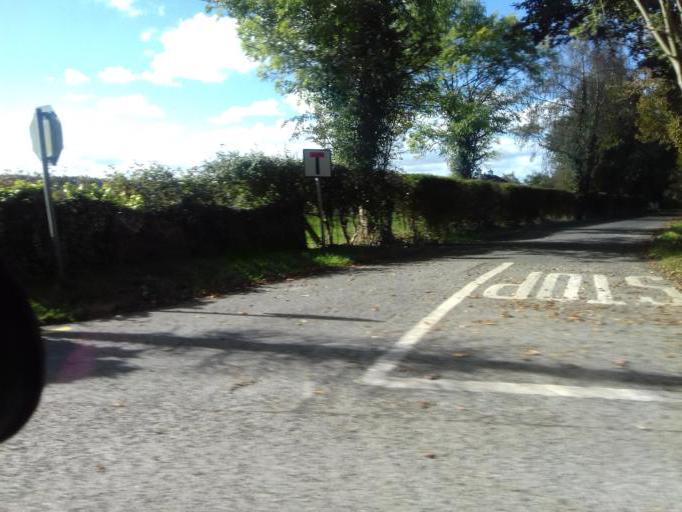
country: IE
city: Kentstown
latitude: 53.6271
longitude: -6.4901
